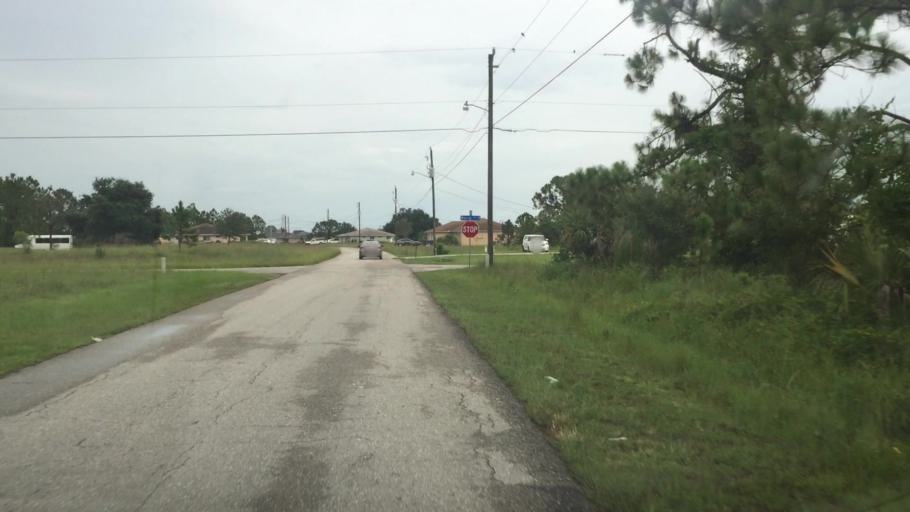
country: US
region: Florida
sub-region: Lee County
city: Gateway
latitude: 26.5895
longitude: -81.7185
